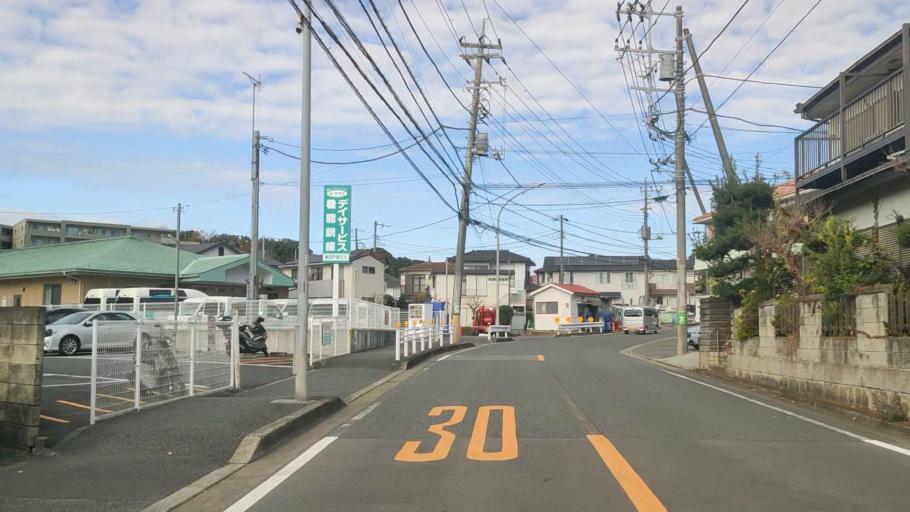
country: JP
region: Kanagawa
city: Yokohama
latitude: 35.4326
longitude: 139.5488
